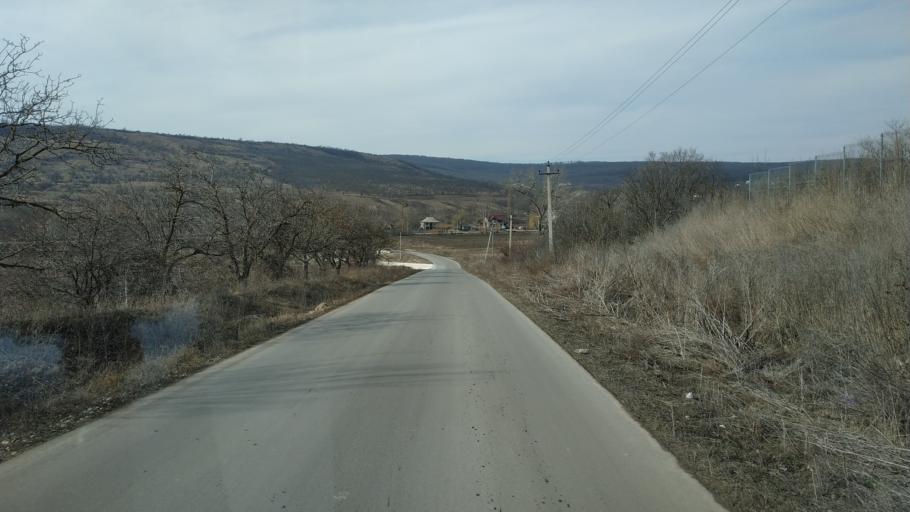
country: MD
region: Nisporeni
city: Nisporeni
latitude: 47.1472
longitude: 28.1141
